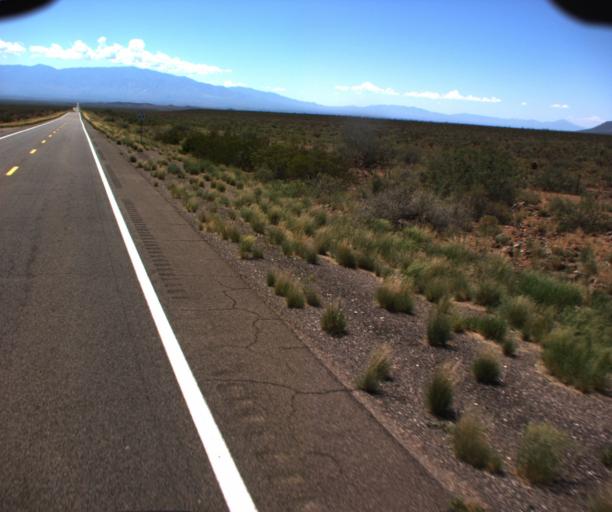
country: US
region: Arizona
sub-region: Greenlee County
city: Morenci
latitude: 32.8411
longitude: -109.4238
